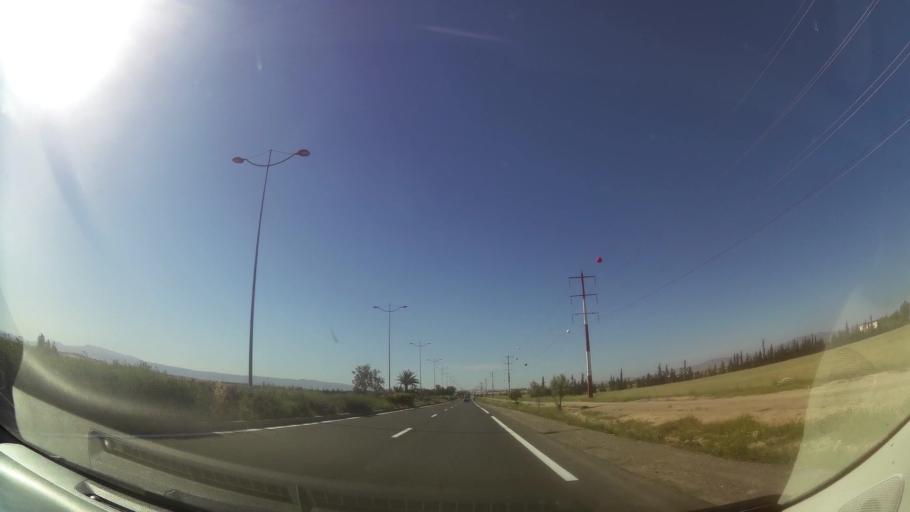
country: MA
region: Oriental
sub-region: Oujda-Angad
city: Oujda
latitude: 34.7507
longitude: -1.9334
